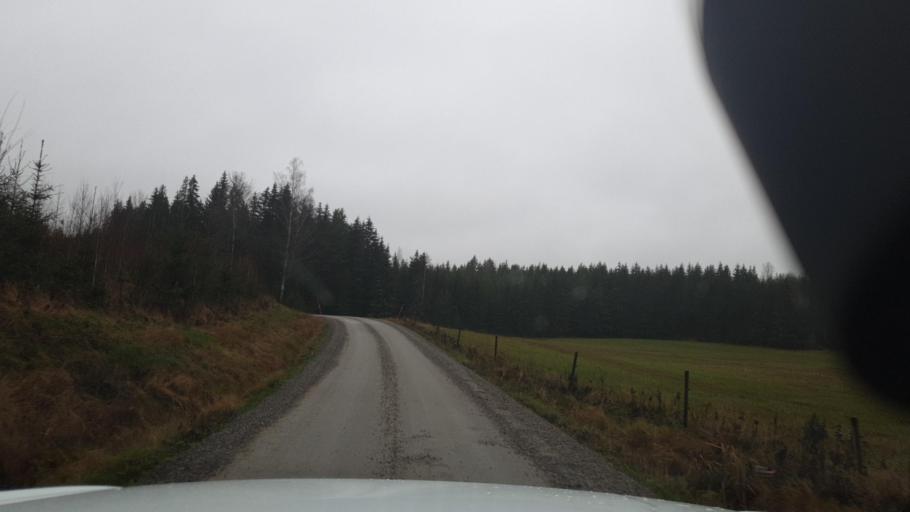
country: SE
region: Vaermland
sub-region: Arvika Kommun
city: Arvika
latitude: 59.5954
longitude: 12.7960
